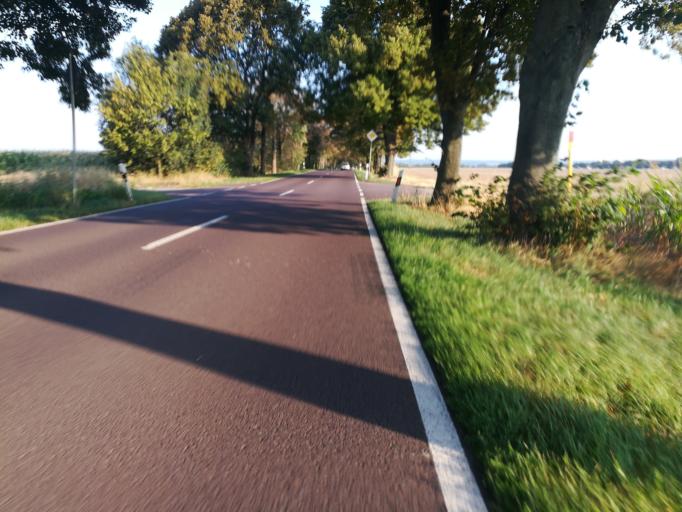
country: DE
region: Saxony-Anhalt
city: Haldensleben I
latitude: 52.2468
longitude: 11.4359
